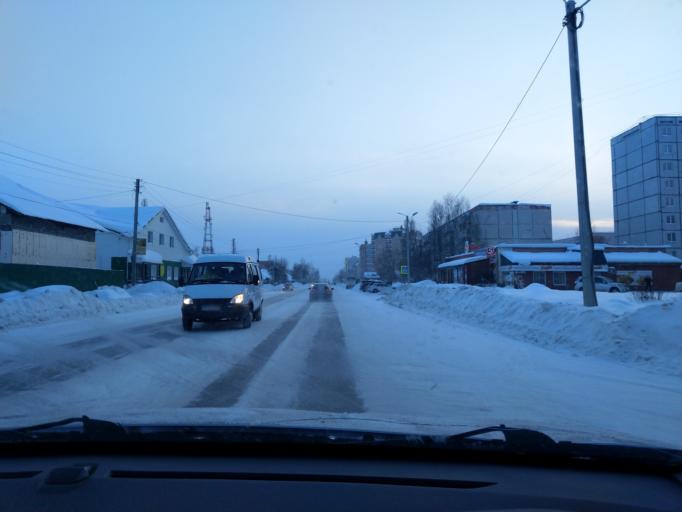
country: RU
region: Perm
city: Dobryanka
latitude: 58.4702
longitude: 56.4059
